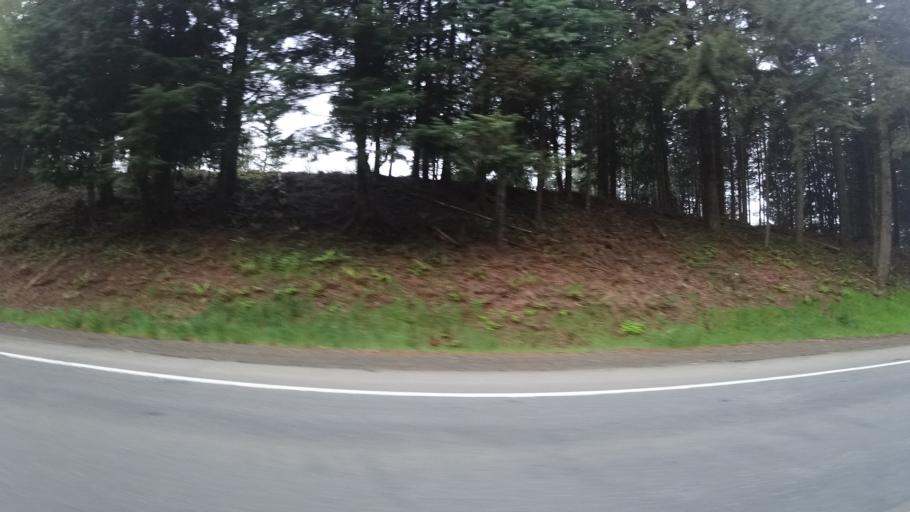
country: US
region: Oregon
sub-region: Coos County
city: Bunker Hill
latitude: 43.2891
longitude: -124.2250
